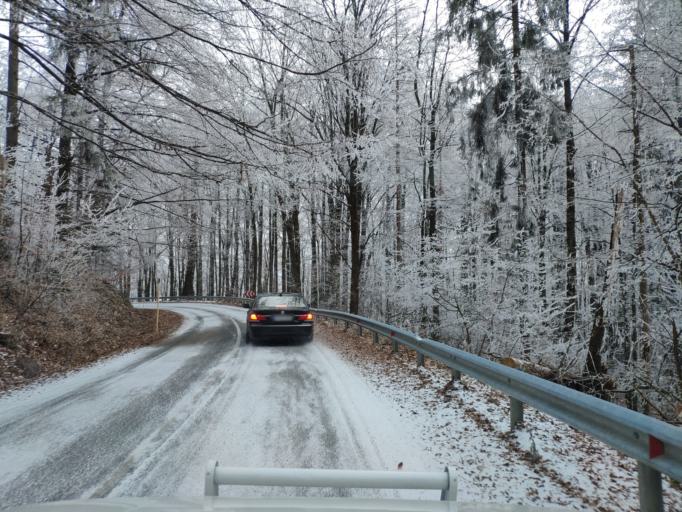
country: SK
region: Kosicky
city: Dobsina
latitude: 48.8011
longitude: 20.4937
